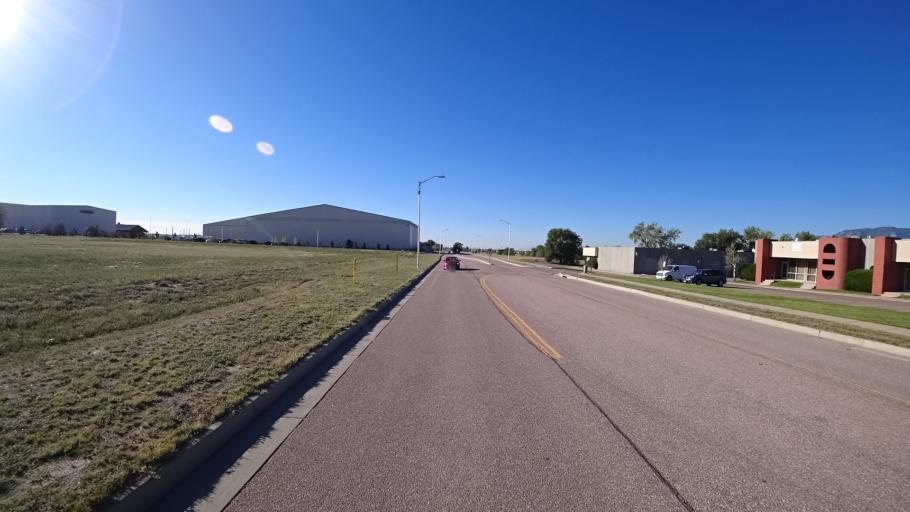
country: US
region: Colorado
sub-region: El Paso County
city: Cimarron Hills
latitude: 38.8095
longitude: -104.7237
